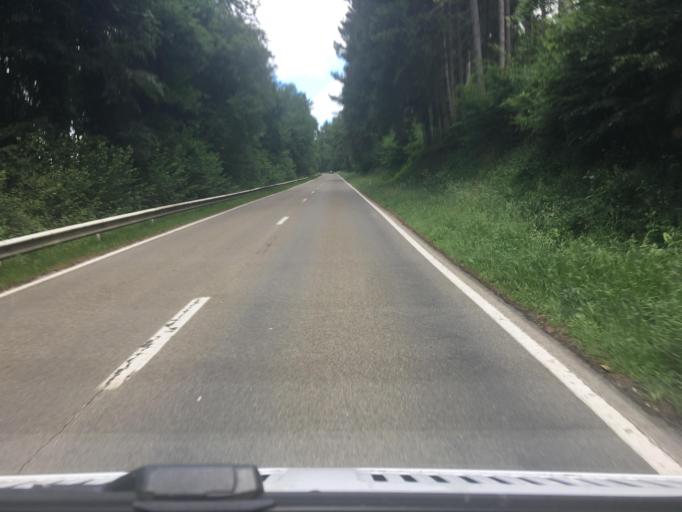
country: BE
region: Wallonia
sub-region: Province du Luxembourg
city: Florenville
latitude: 49.6365
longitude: 5.3450
